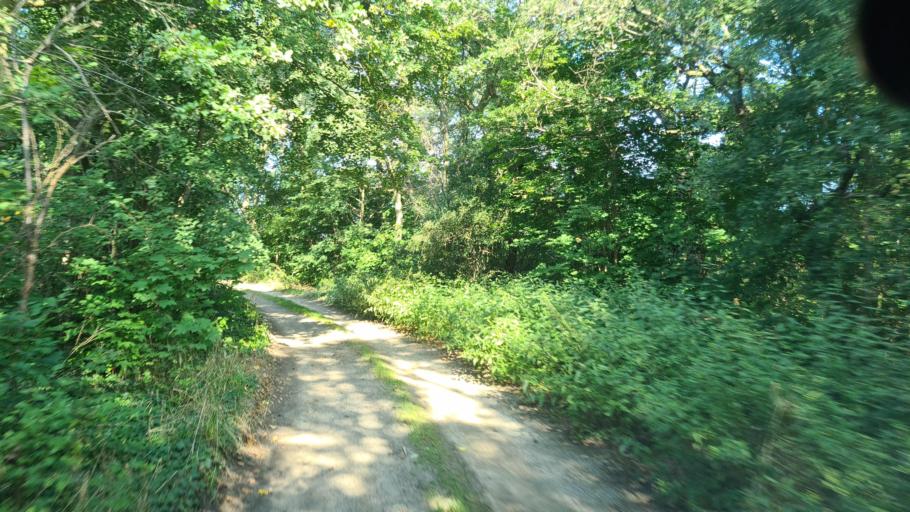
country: DE
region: Brandenburg
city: Luckau
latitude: 51.8439
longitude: 13.6871
